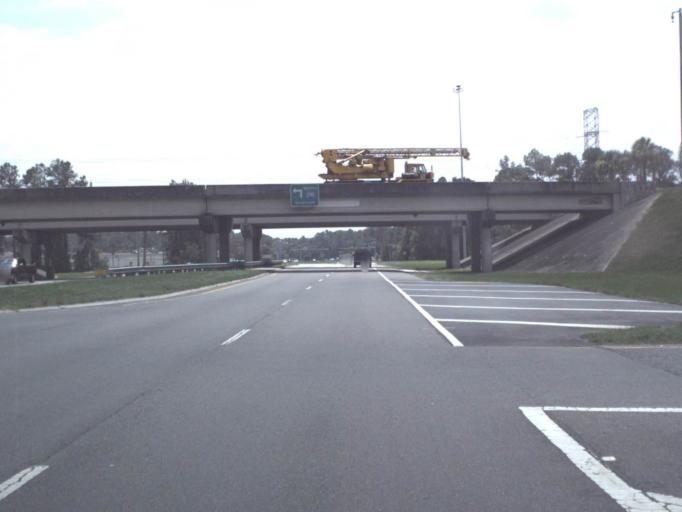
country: US
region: Florida
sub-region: Nassau County
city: Nassau Village-Ratliff
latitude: 30.4558
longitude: -81.7061
